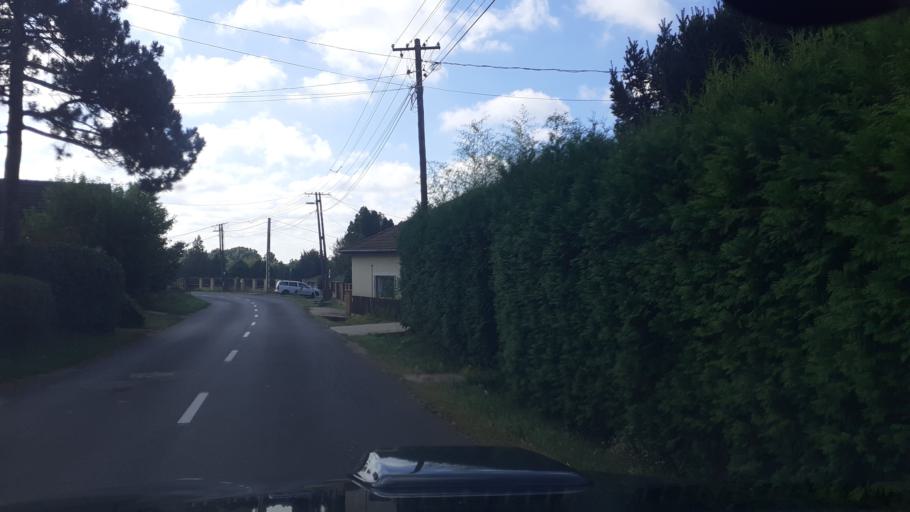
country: HU
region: Fejer
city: Baracs
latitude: 46.8951
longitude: 18.8982
